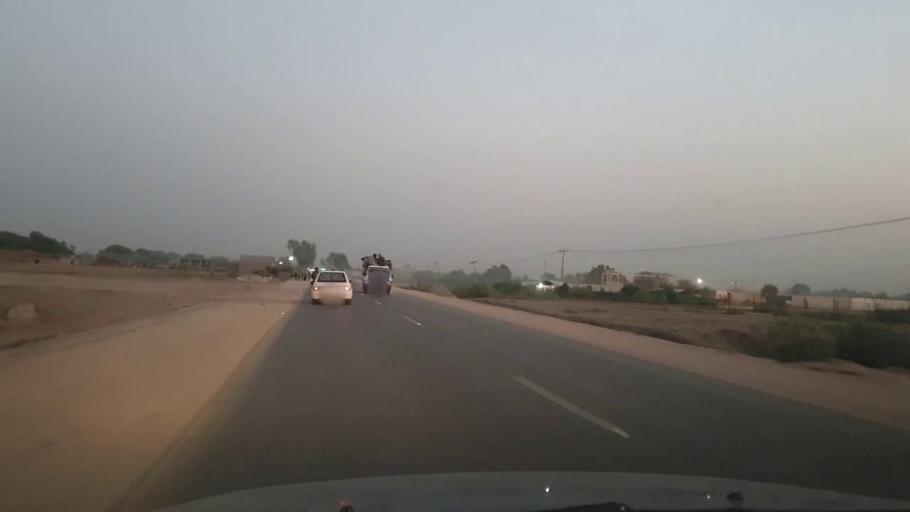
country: PK
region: Sindh
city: Tando Allahyar
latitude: 25.4358
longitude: 68.7422
